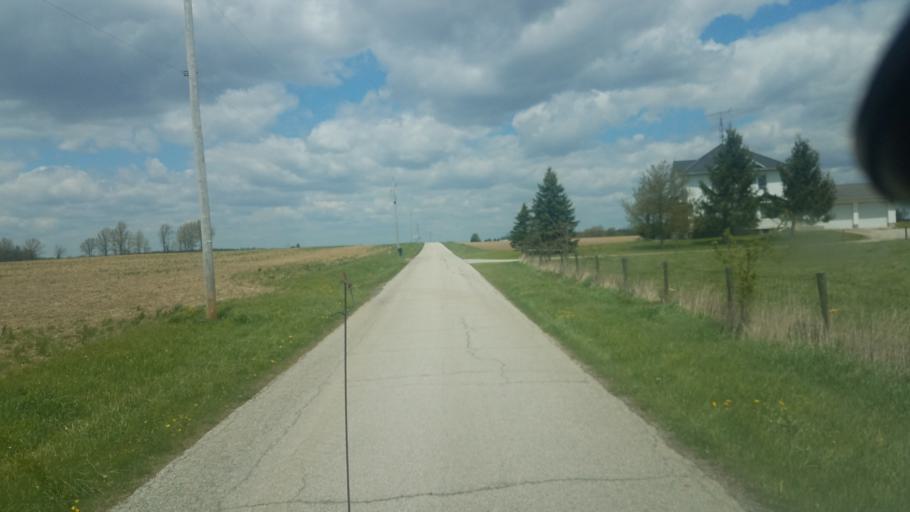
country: US
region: Ohio
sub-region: Crawford County
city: Bucyrus
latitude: 40.7294
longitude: -82.9358
